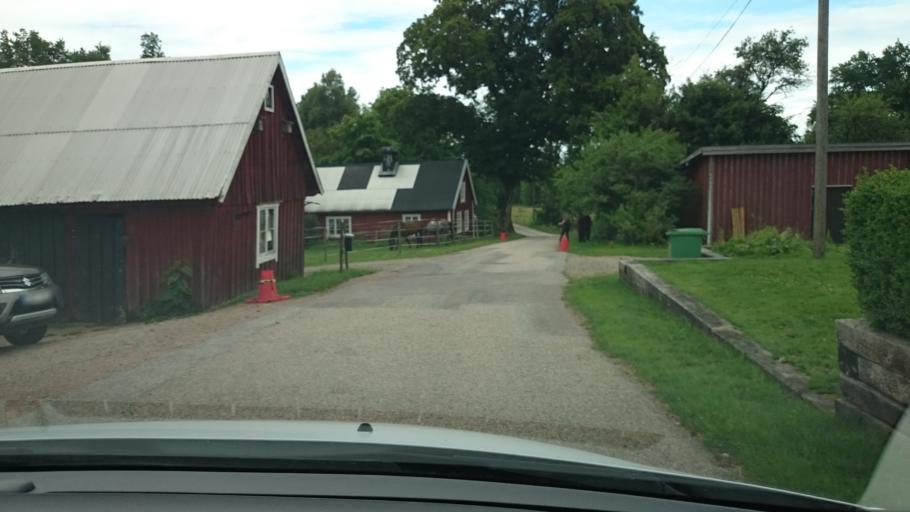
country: SE
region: Halland
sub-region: Hylte Kommun
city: Hyltebruk
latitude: 56.9666
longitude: 13.1971
